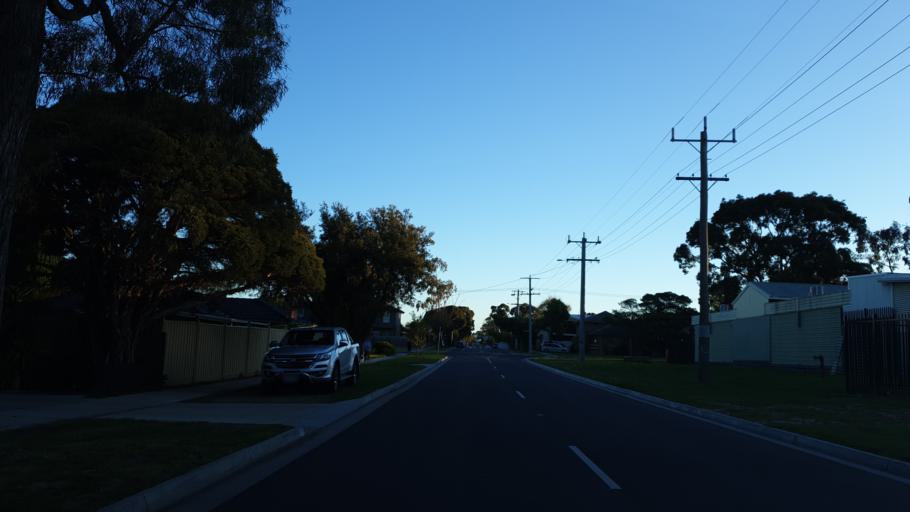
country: AU
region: Victoria
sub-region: Casey
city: Cranbourne
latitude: -38.1078
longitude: 145.2883
